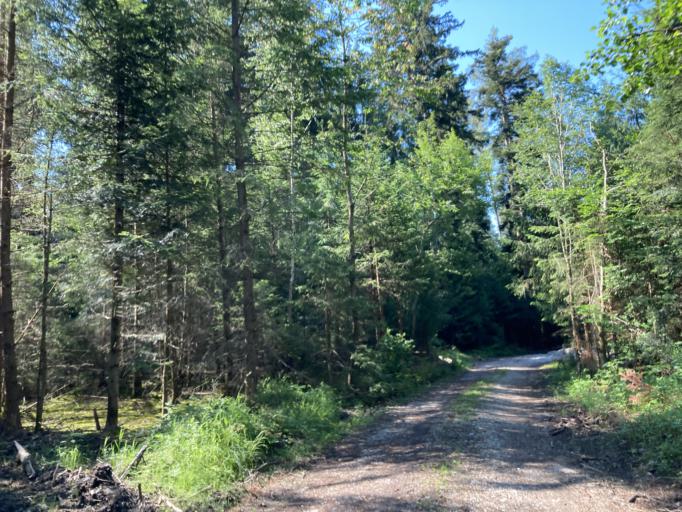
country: DE
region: Bavaria
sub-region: Upper Bavaria
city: Hoslwang
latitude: 47.9646
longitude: 12.3055
